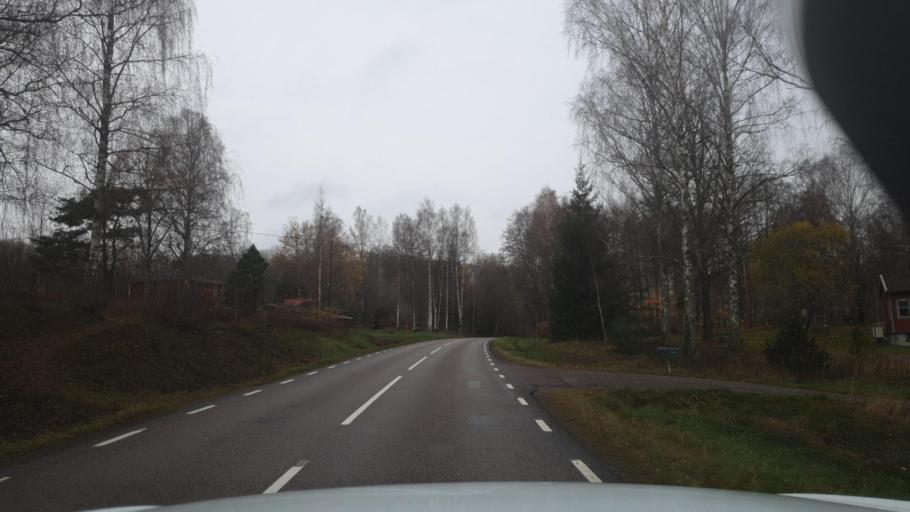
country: SE
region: Vaermland
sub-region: Arvika Kommun
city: Arvika
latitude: 59.4828
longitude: 12.7012
